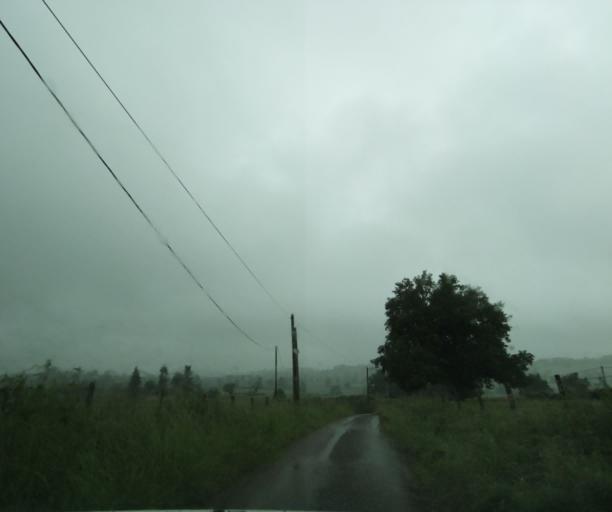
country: FR
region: Bourgogne
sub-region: Departement de Saone-et-Loire
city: La Clayette
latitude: 46.3459
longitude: 4.2338
